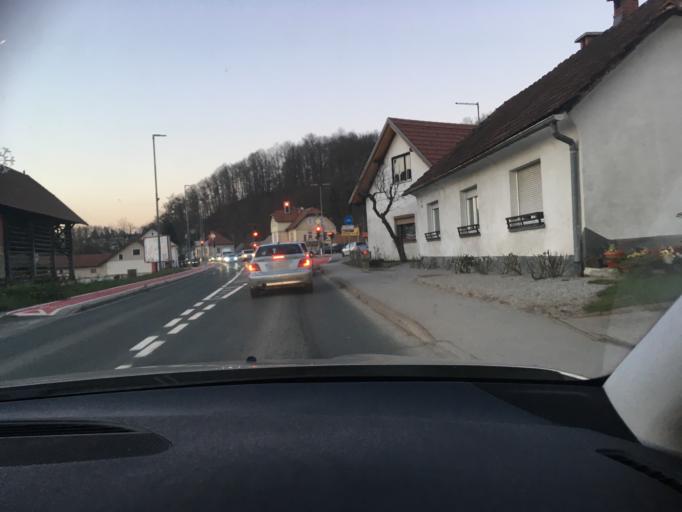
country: SI
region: Skofljica
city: Skofljica
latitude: 45.9825
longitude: 14.5757
